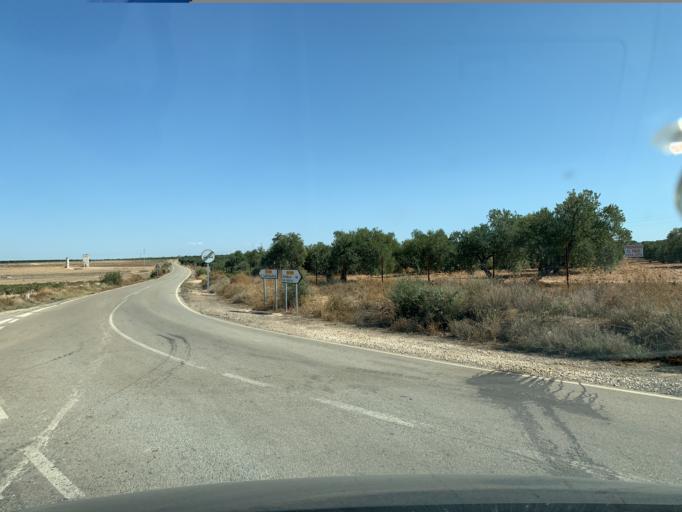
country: ES
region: Andalusia
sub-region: Provincia de Sevilla
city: La Lantejuela
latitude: 37.3383
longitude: -5.2869
